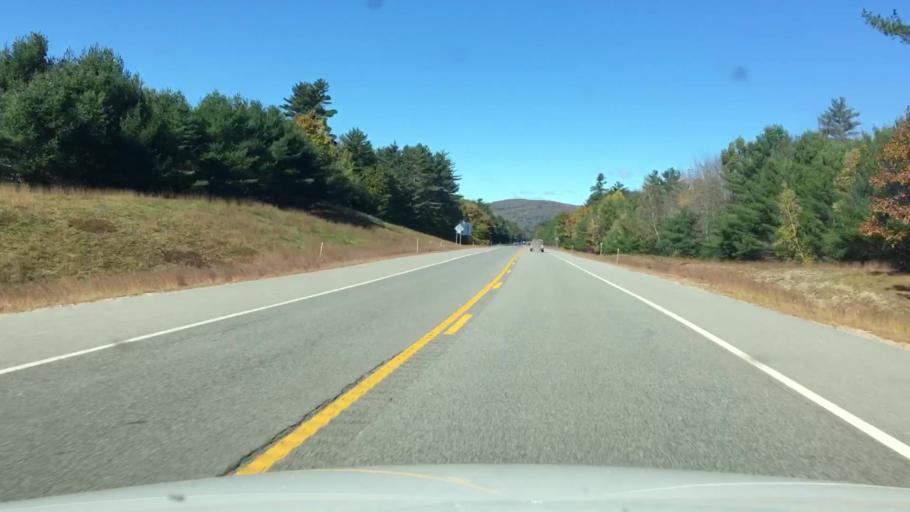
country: US
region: New Hampshire
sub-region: Carroll County
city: Sanbornville
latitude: 43.4854
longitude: -71.0079
